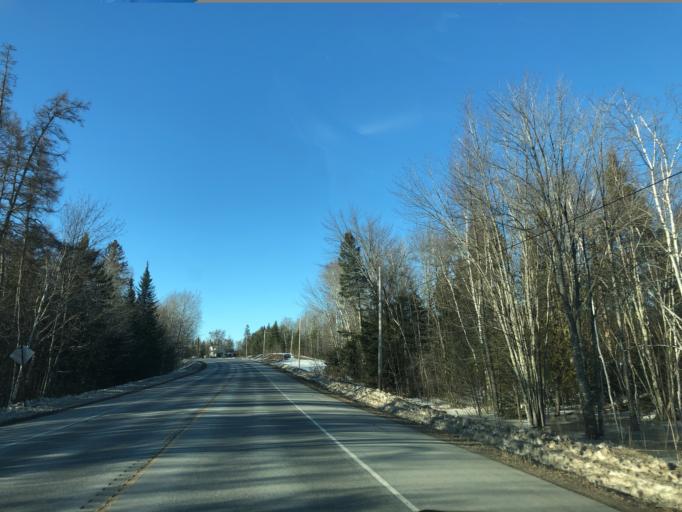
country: US
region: Maine
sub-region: Penobscot County
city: Kenduskeag
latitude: 44.9447
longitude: -68.9452
